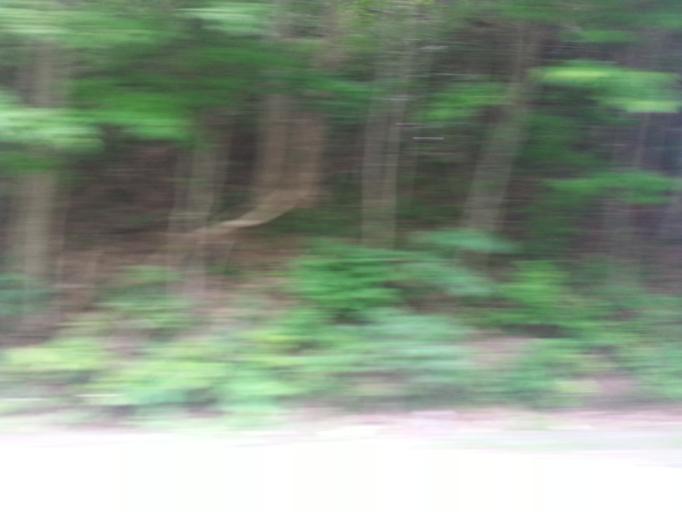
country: US
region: Georgia
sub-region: Towns County
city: Hiawassee
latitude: 34.8587
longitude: -83.8016
